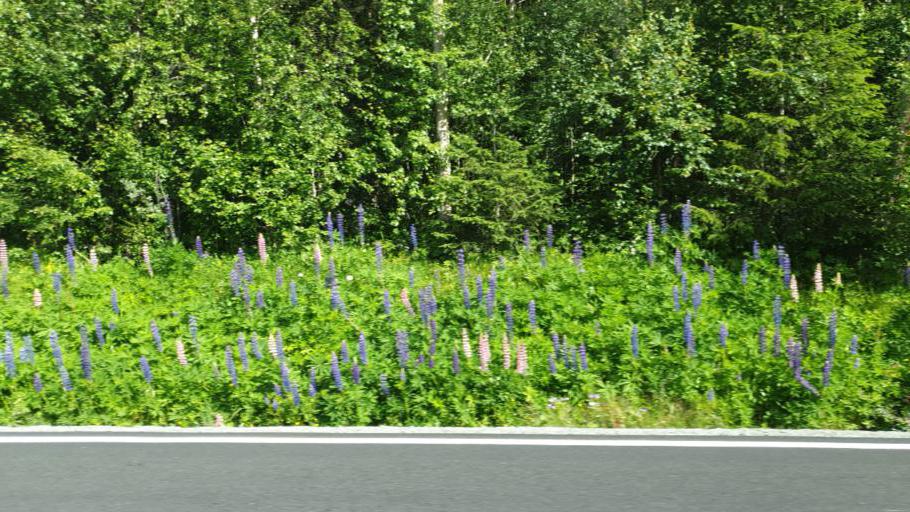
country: NO
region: Oppland
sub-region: Oystre Slidre
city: Heggenes
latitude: 61.1772
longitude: 8.9960
